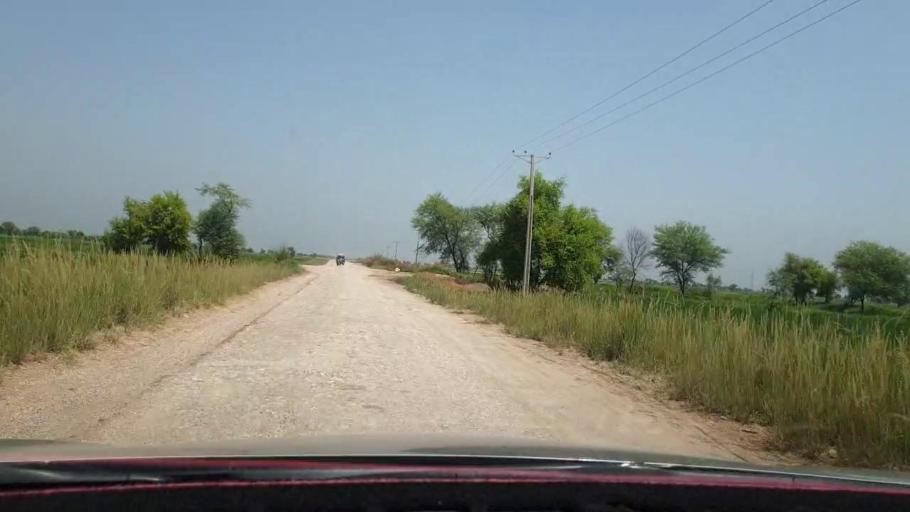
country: PK
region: Sindh
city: Warah
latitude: 27.4352
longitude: 67.7241
